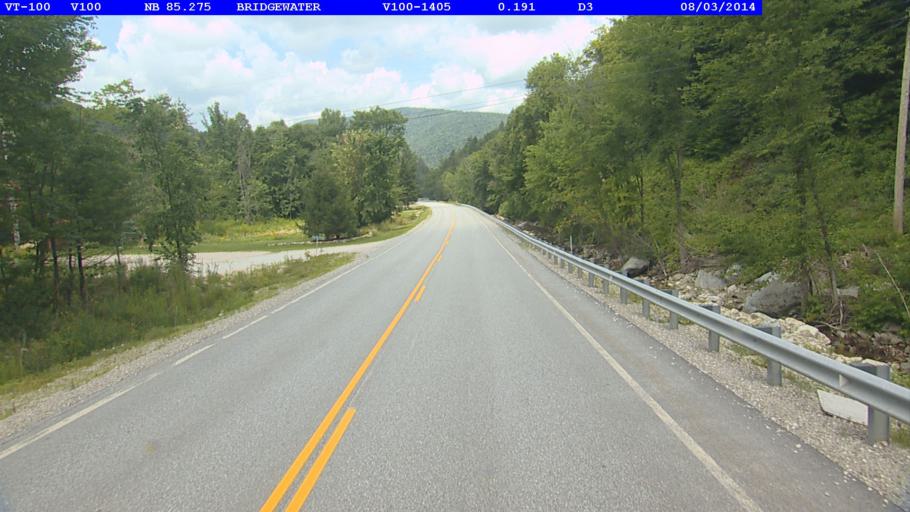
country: US
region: Vermont
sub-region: Rutland County
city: Rutland
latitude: 43.5897
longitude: -72.7548
